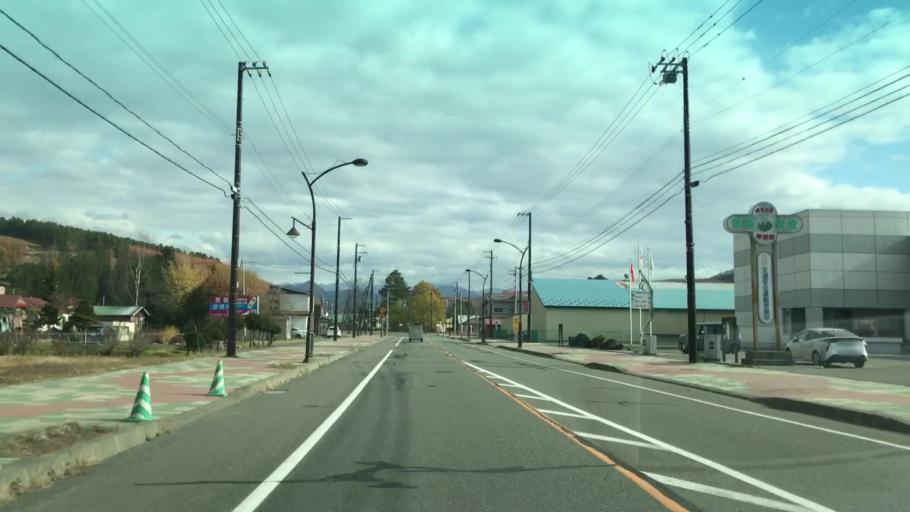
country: JP
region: Hokkaido
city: Shizunai-furukawacho
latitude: 42.7264
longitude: 142.3015
